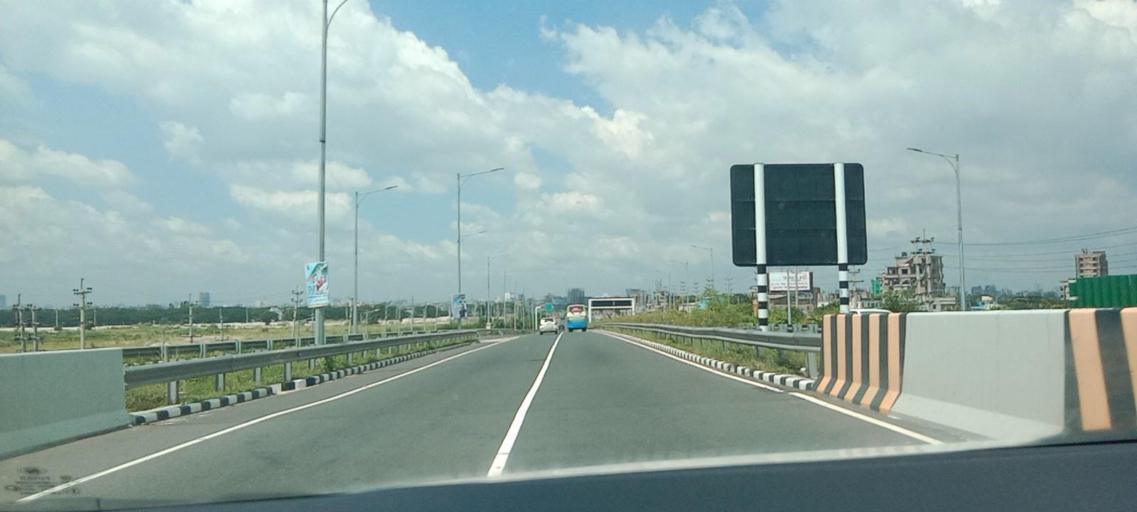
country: BD
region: Dhaka
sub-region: Dhaka
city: Dhaka
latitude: 23.6758
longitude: 90.4060
